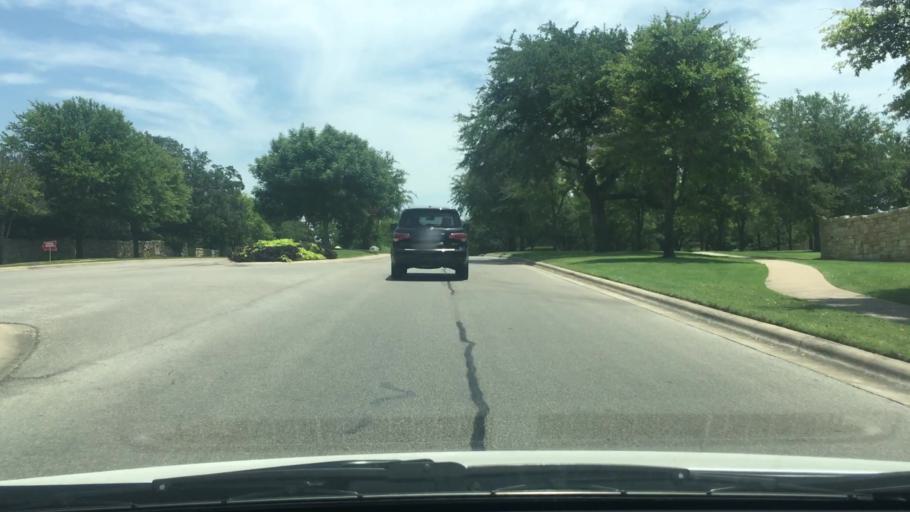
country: US
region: Texas
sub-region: Williamson County
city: Anderson Mill
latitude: 30.4684
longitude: -97.8479
